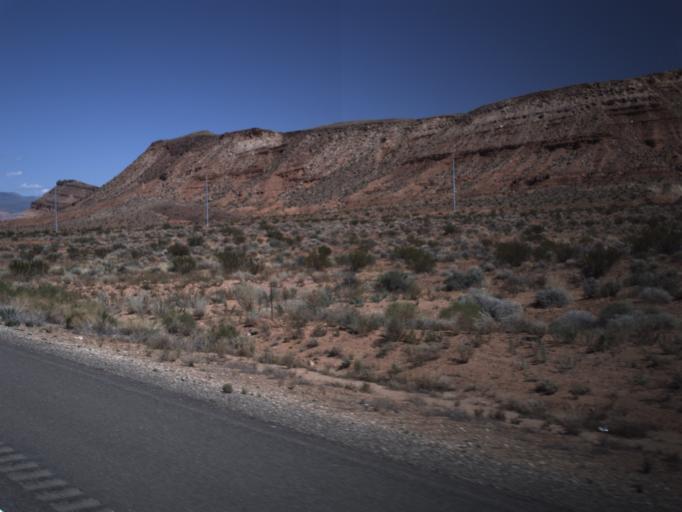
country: US
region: Utah
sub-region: Washington County
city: Washington
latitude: 37.0438
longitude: -113.4856
